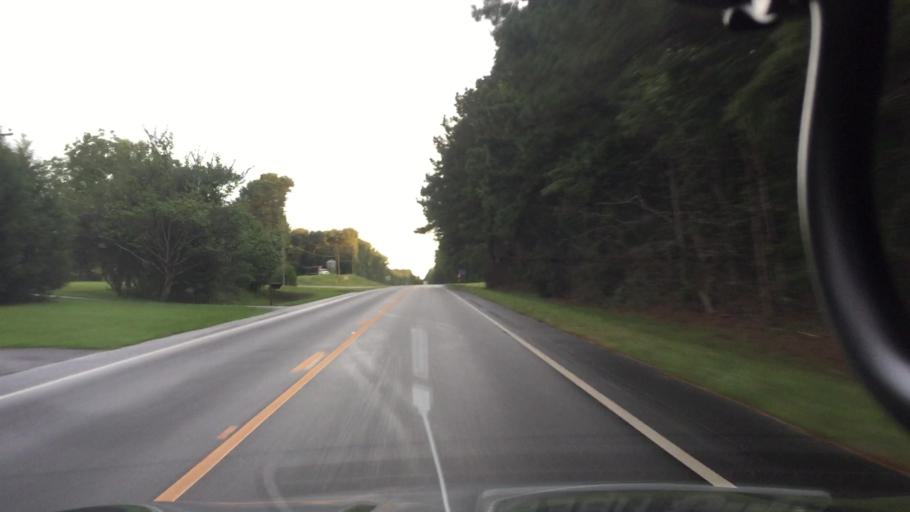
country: US
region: Alabama
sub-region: Coffee County
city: New Brockton
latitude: 31.5350
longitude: -85.9183
